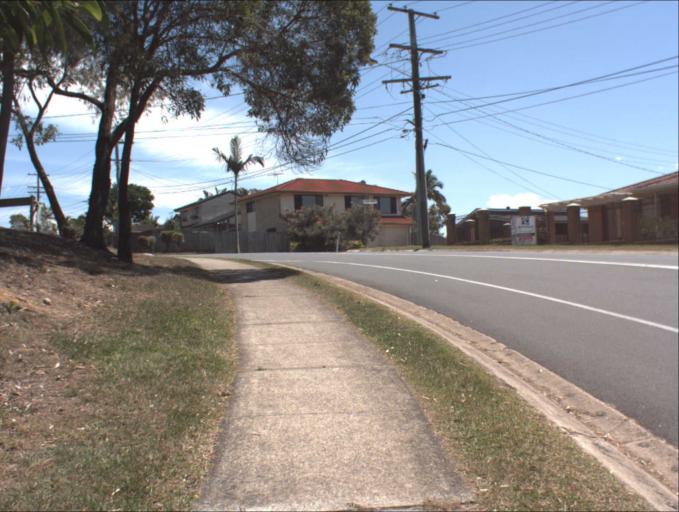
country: AU
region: Queensland
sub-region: Logan
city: Springwood
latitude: -27.6076
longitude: 153.1335
